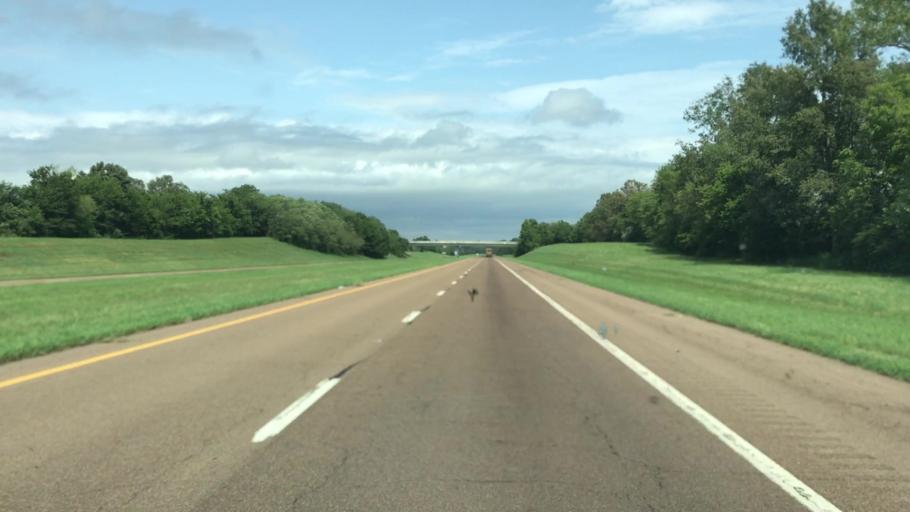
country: US
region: Tennessee
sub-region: Obion County
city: South Fulton
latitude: 36.4878
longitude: -88.9289
